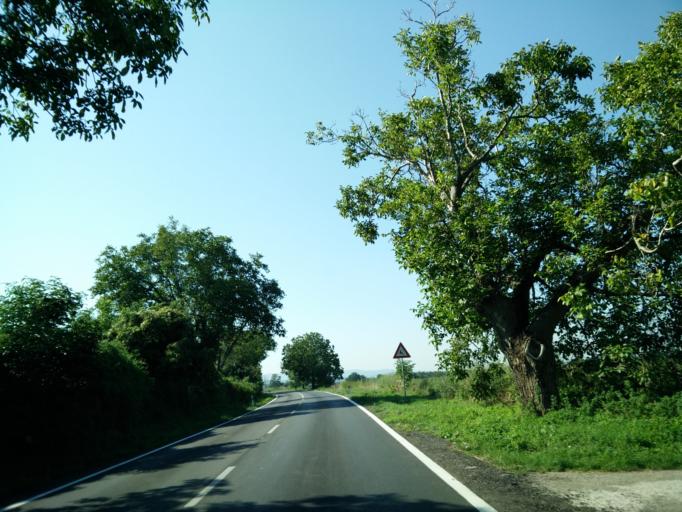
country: SK
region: Nitriansky
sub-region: Okres Nitra
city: Nitra
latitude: 48.4630
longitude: 18.1435
